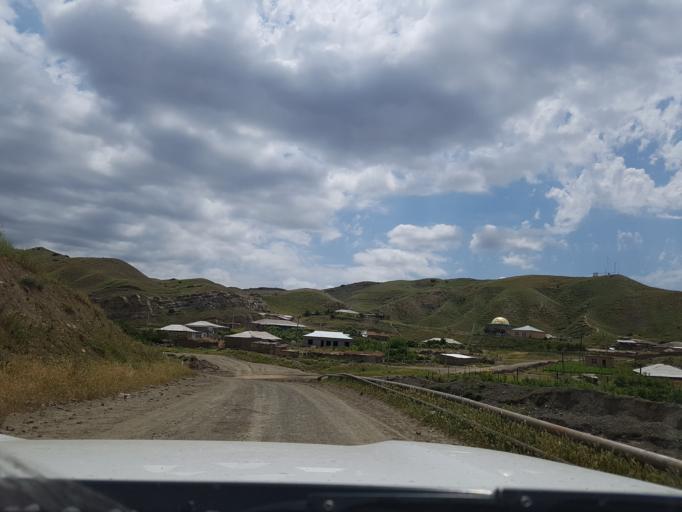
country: TM
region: Ahal
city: Baharly
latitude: 38.2020
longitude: 57.0035
